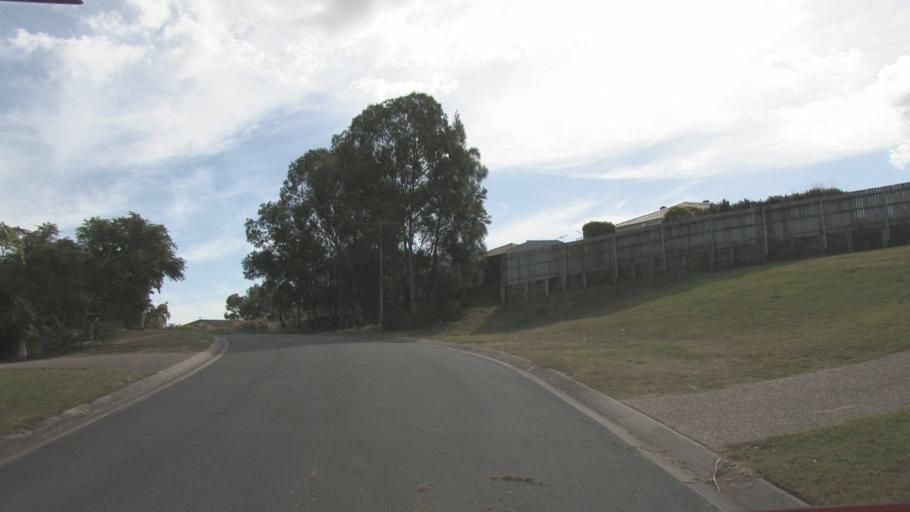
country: AU
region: Queensland
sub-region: Logan
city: Beenleigh
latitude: -27.7099
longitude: 153.1673
